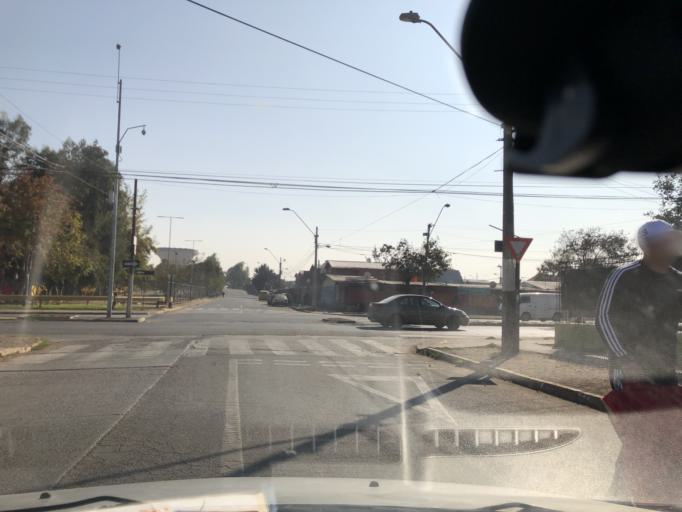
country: CL
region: Santiago Metropolitan
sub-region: Provincia de Cordillera
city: Puente Alto
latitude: -33.6196
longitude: -70.5948
